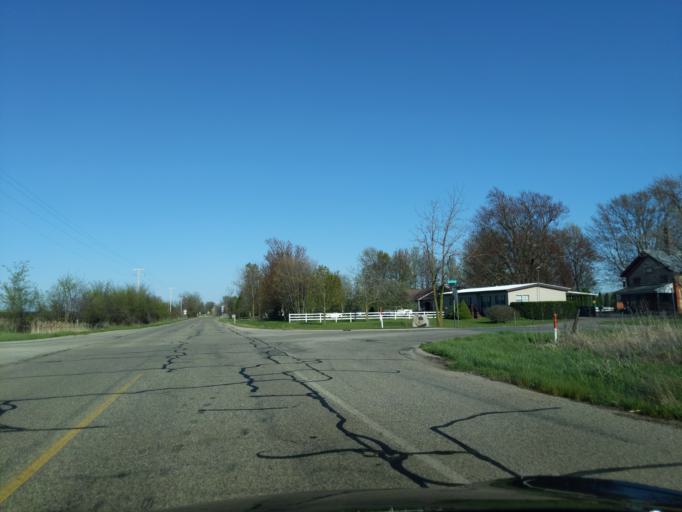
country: US
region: Michigan
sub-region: Ionia County
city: Portland
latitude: 42.8858
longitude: -84.9954
